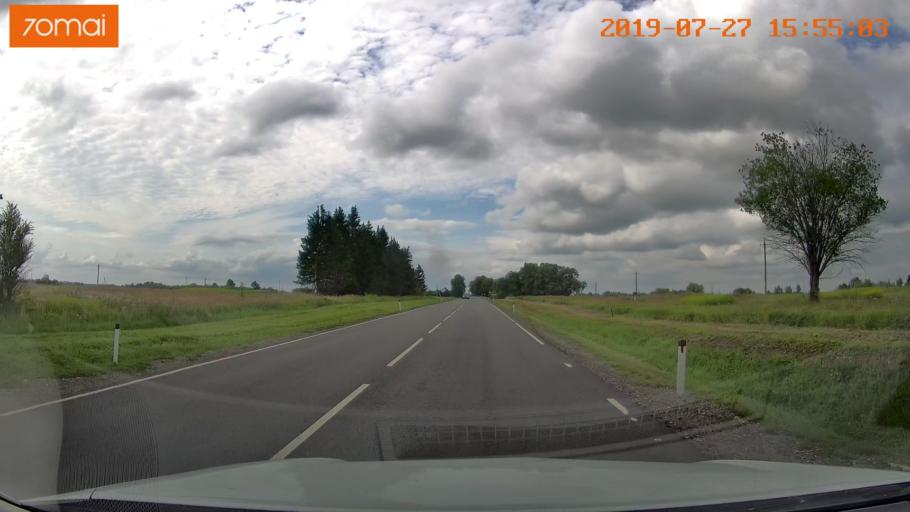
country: RU
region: Kaliningrad
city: Chernyakhovsk
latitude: 54.6114
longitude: 21.9277
